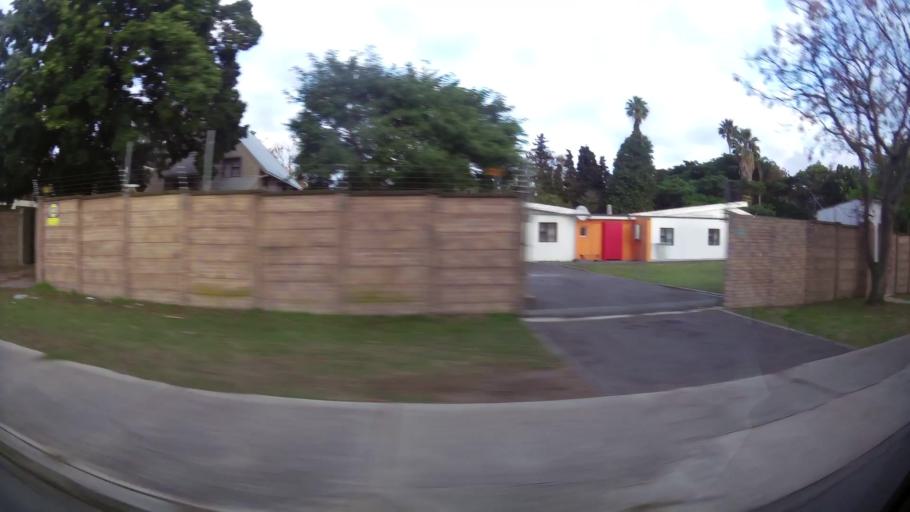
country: ZA
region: Eastern Cape
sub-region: Nelson Mandela Bay Metropolitan Municipality
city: Port Elizabeth
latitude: -33.9823
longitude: 25.5810
